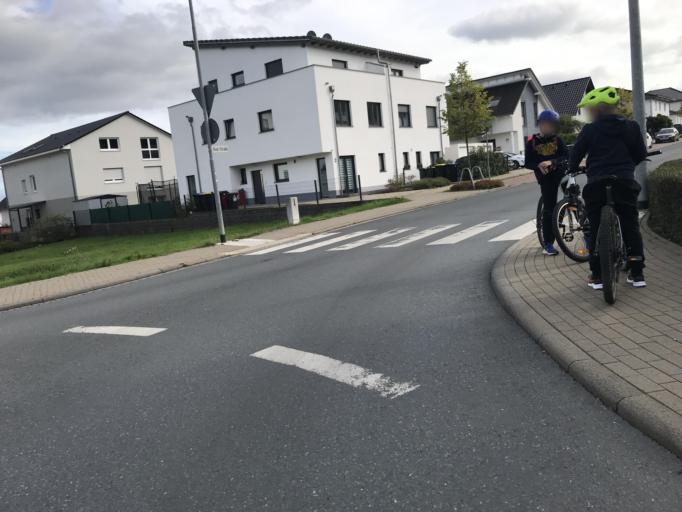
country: DE
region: Hesse
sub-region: Regierungsbezirk Darmstadt
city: Butzbach
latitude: 50.4406
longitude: 8.6549
